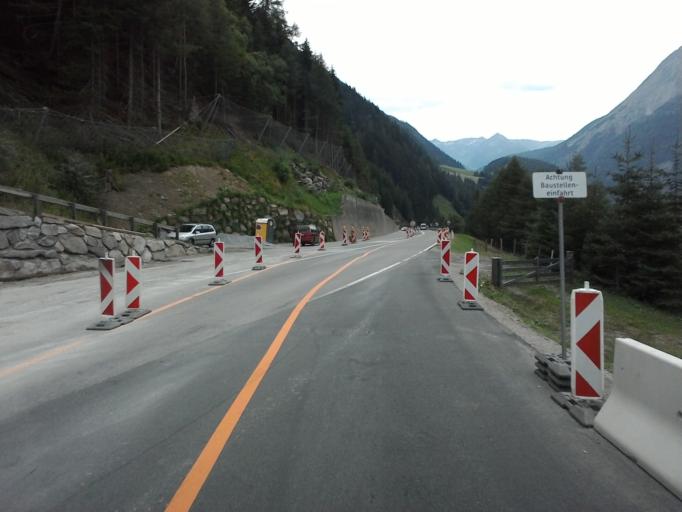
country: AT
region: Tyrol
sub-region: Politischer Bezirk Lienz
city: Matrei in Osttirol
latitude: 47.0716
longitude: 12.5324
